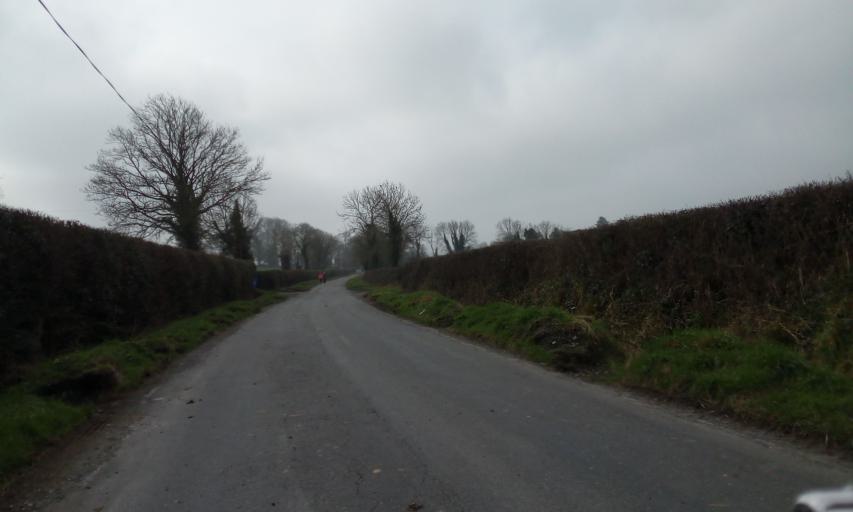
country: IE
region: Leinster
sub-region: Kilkenny
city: Kilkenny
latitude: 52.6680
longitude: -7.1856
